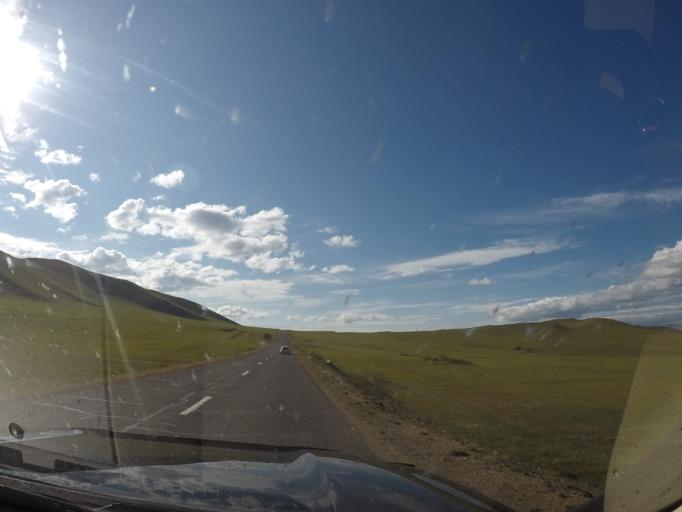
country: MN
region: Hentiy
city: Modot
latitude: 47.7479
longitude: 108.9700
